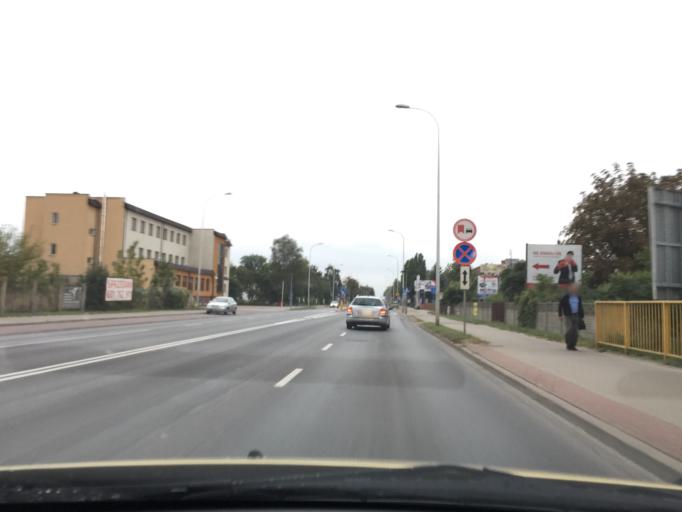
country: PL
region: Greater Poland Voivodeship
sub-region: Kalisz
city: Kalisz
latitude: 51.7433
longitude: 18.0649
